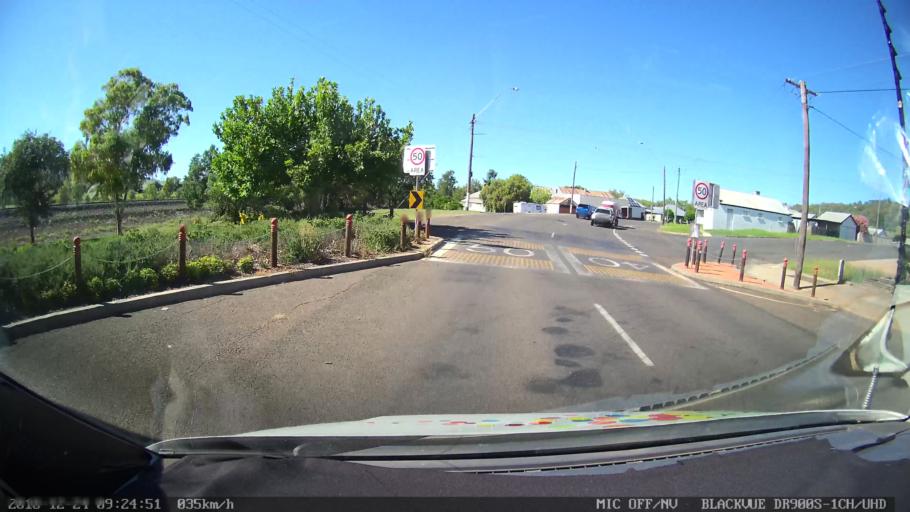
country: AU
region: New South Wales
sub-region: Liverpool Plains
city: Quirindi
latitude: -31.5119
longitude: 150.6792
